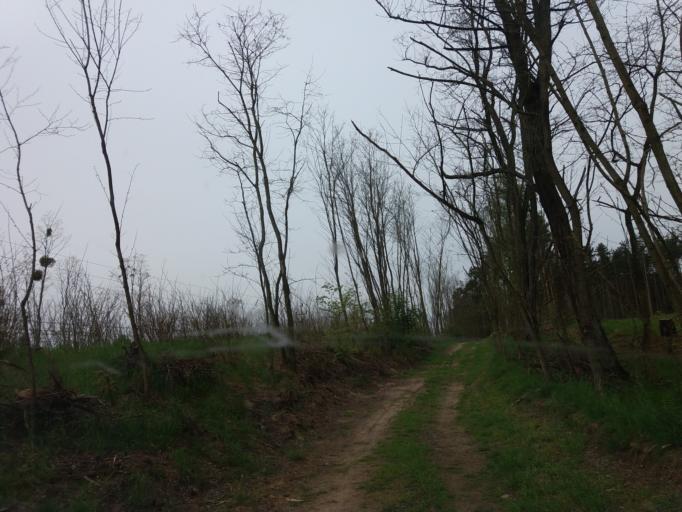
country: PL
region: West Pomeranian Voivodeship
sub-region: Powiat choszczenski
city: Bierzwnik
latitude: 53.0082
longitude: 15.6901
